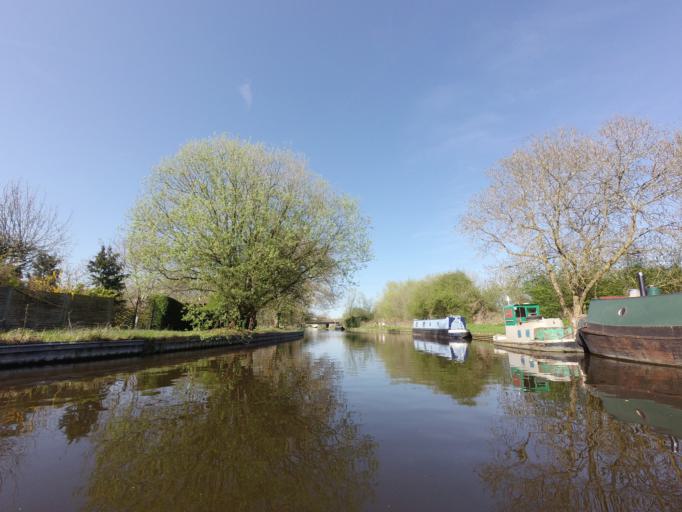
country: GB
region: England
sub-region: Greater London
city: Uxbridge
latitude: 51.5582
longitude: -0.4830
